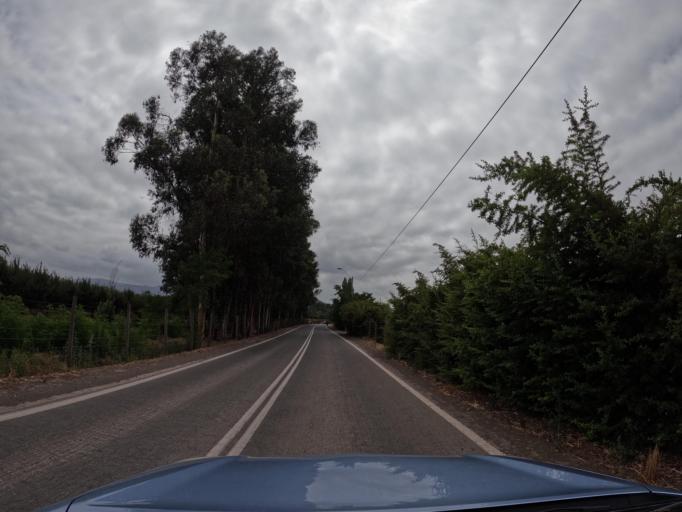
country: CL
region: Maule
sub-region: Provincia de Curico
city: Teno
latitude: -34.7585
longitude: -71.2095
